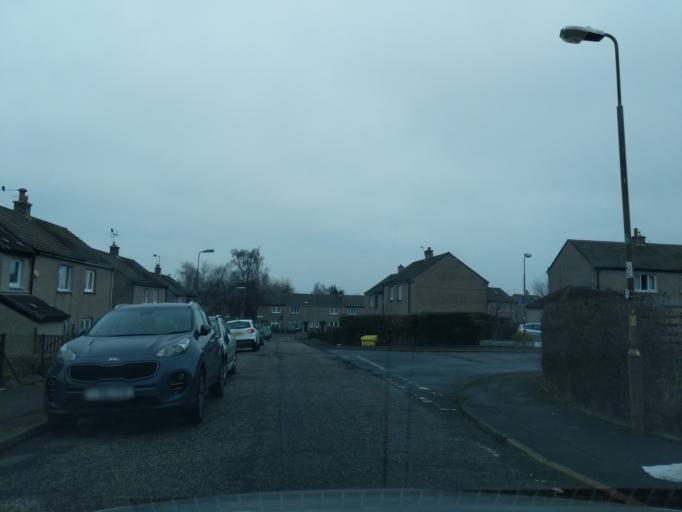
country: GB
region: Scotland
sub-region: Edinburgh
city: Currie
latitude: 55.8935
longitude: -3.3237
